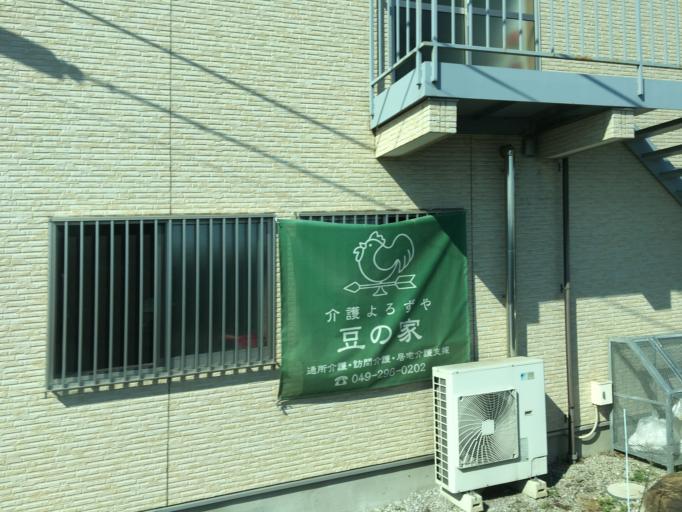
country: JP
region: Saitama
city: Morohongo
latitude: 35.9765
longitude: 139.3366
